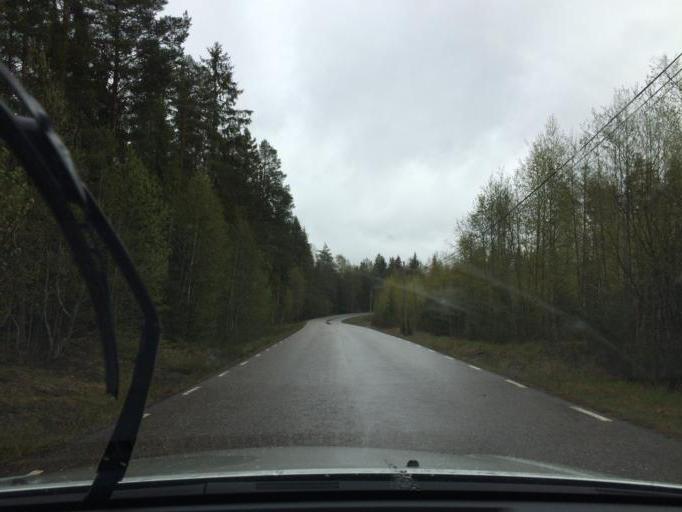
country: SE
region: Dalarna
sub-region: Ludvika Kommun
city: Grangesberg
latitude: 60.0632
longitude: 14.8779
